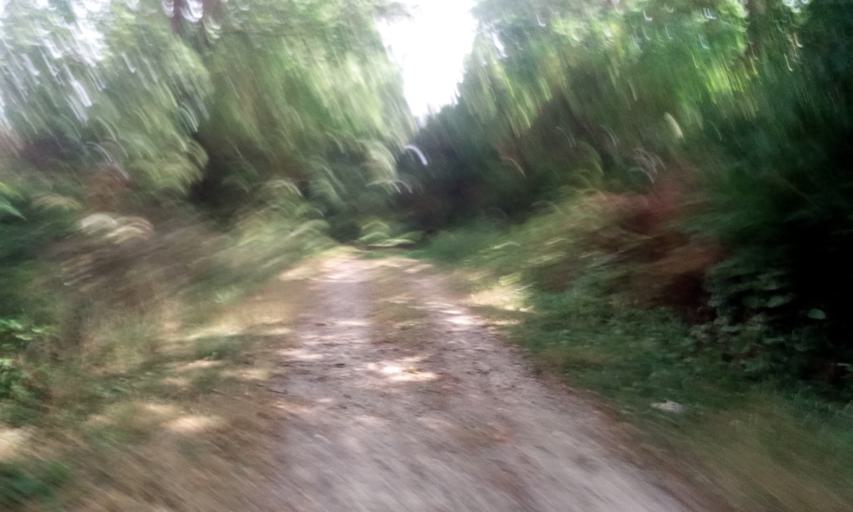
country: FR
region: Lower Normandy
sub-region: Departement du Calvados
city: Douvres-la-Delivrande
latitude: 49.2951
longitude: -0.4017
